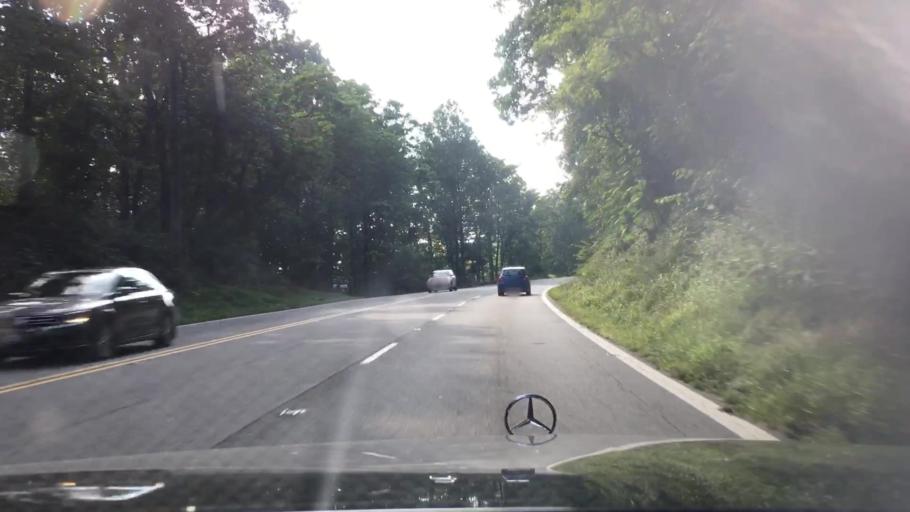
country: US
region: Virginia
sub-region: City of Waynesboro
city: Waynesboro
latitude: 38.0375
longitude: -78.8209
